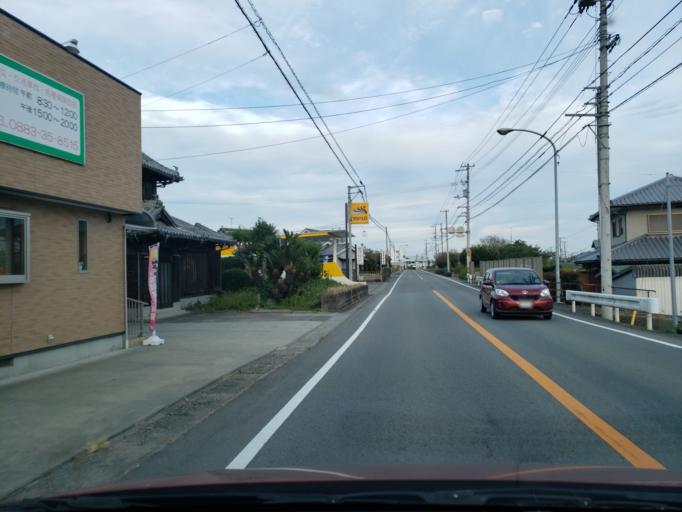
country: JP
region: Tokushima
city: Wakimachi
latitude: 34.0775
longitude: 134.2436
